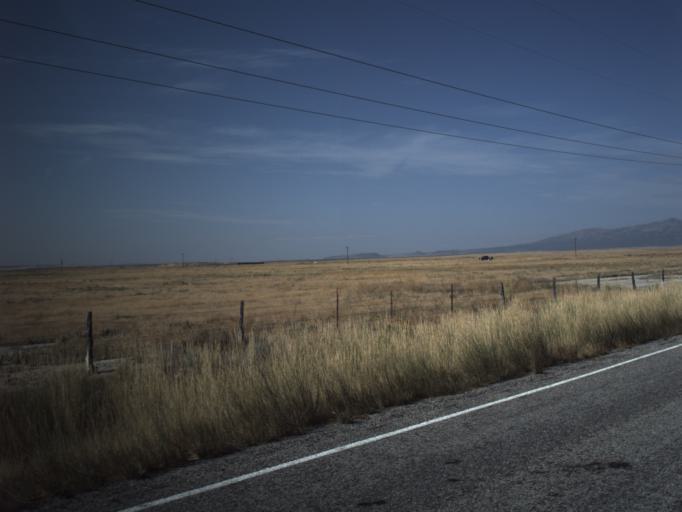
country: US
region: Idaho
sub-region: Oneida County
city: Malad City
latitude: 41.9662
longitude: -112.9562
